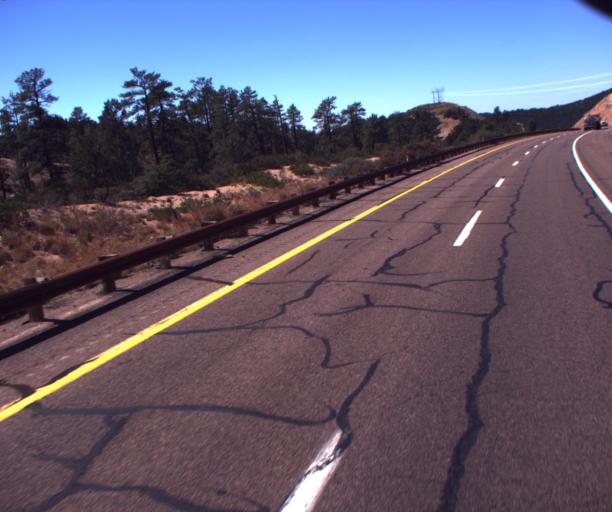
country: US
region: Arizona
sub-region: Gila County
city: Star Valley
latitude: 34.2791
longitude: -111.1566
